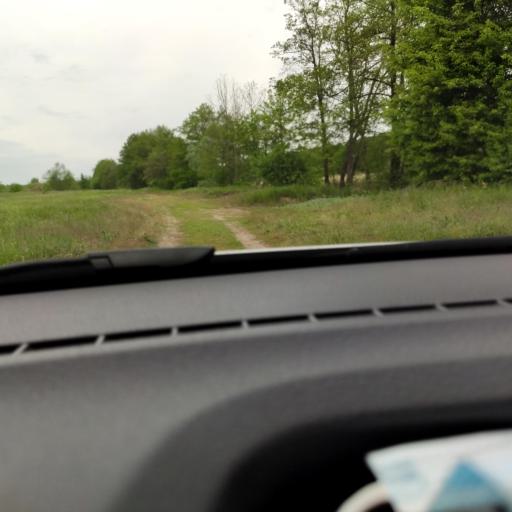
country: RU
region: Voronezj
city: Ramon'
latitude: 51.9364
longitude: 39.3768
